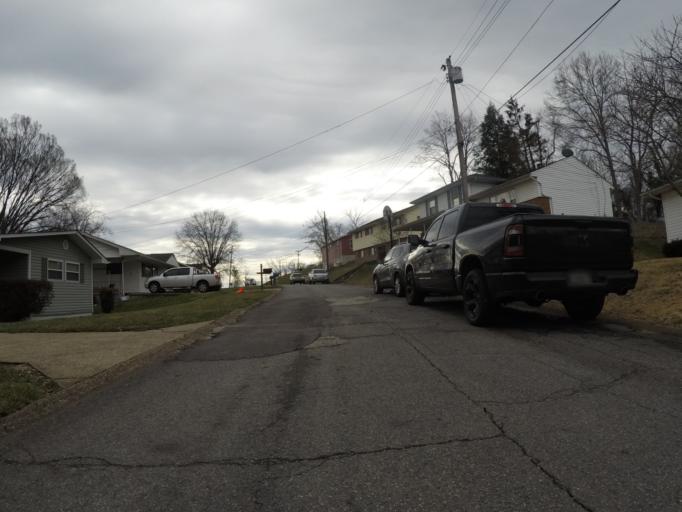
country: US
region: West Virginia
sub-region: Cabell County
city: Pea Ridge
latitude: 38.3962
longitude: -82.3811
